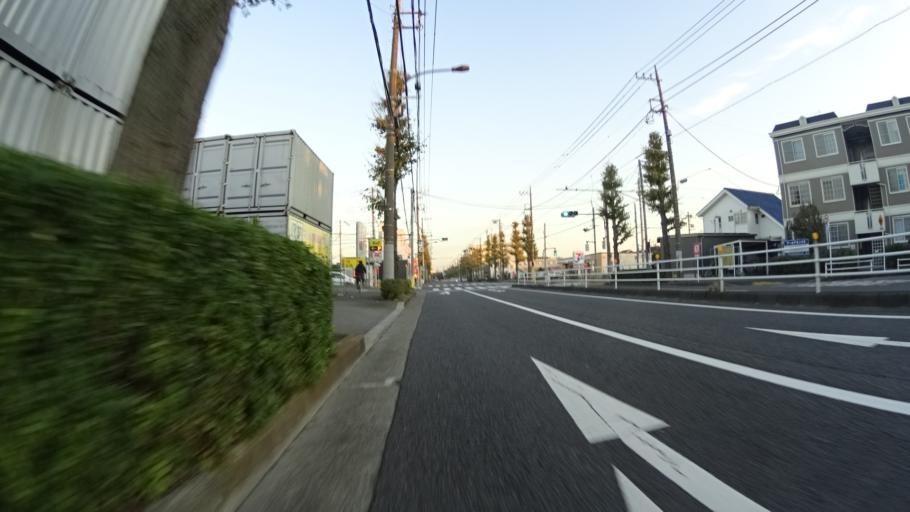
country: JP
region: Tokyo
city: Fussa
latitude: 35.7038
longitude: 139.3544
